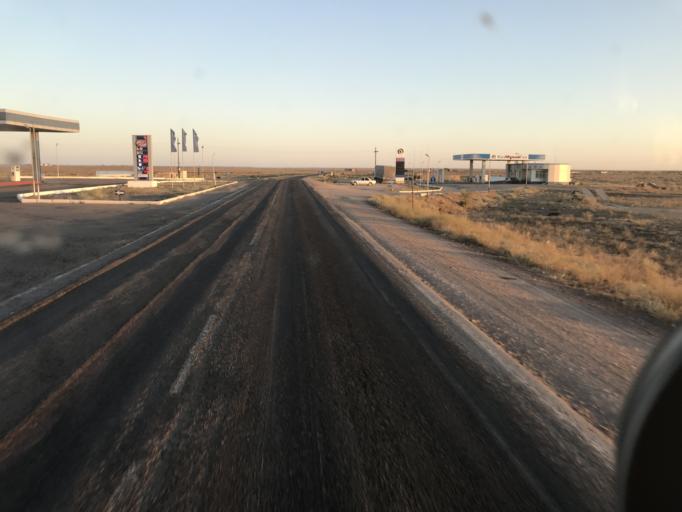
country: KZ
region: Qaraghandy
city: Saryshaghan
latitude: 46.0205
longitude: 73.5915
